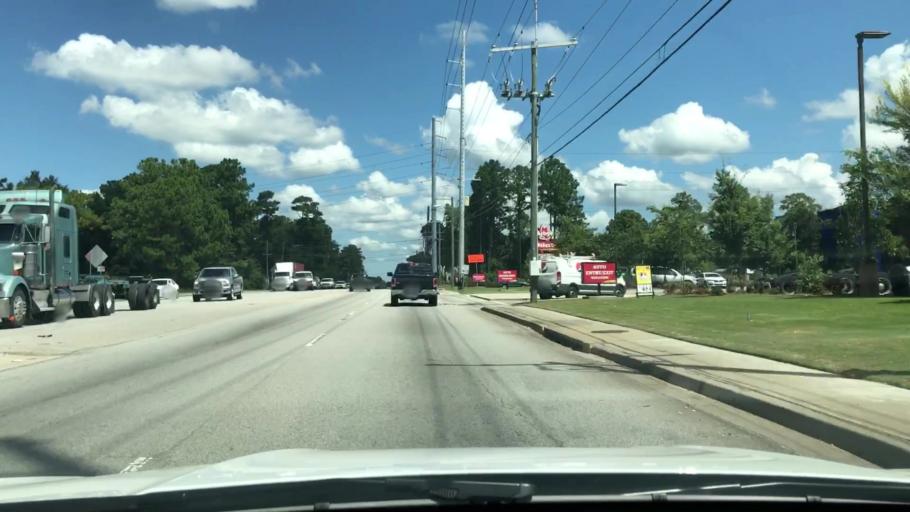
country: US
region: South Carolina
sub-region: Berkeley County
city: Hanahan
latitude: 32.9034
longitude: -79.9856
